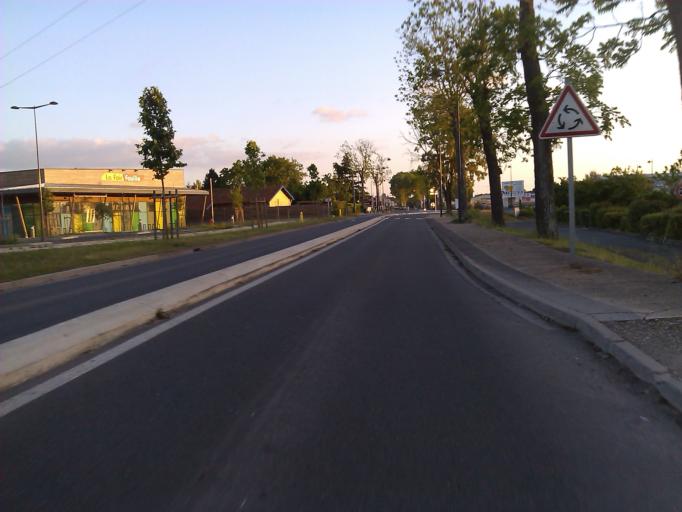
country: FR
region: Aquitaine
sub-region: Departement de la Gironde
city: Ambares-et-Lagrave
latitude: 44.9050
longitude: -0.4884
